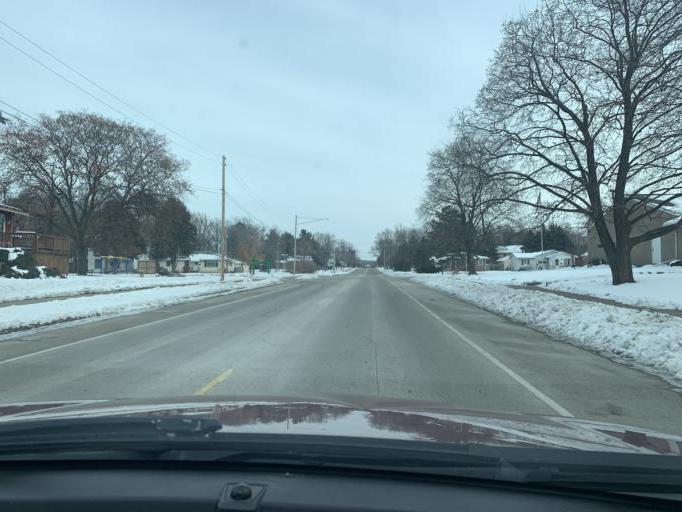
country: US
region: Minnesota
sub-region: Washington County
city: Saint Paul Park
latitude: 44.8366
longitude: -92.9897
